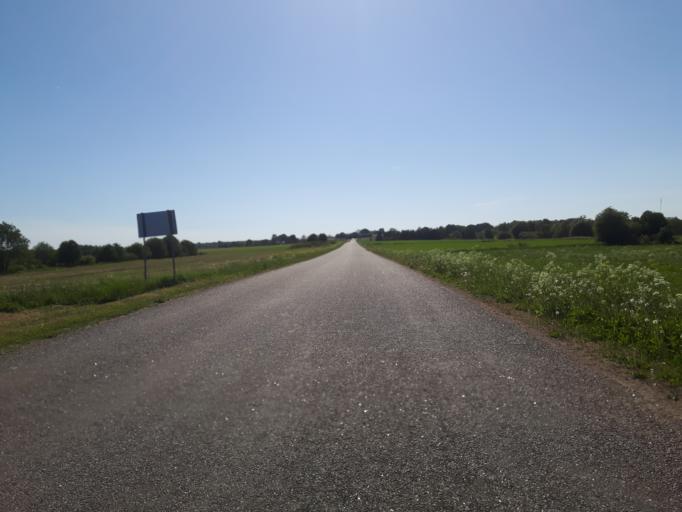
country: EE
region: Laeaene-Virumaa
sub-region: Haljala vald
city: Haljala
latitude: 59.5449
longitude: 26.1693
